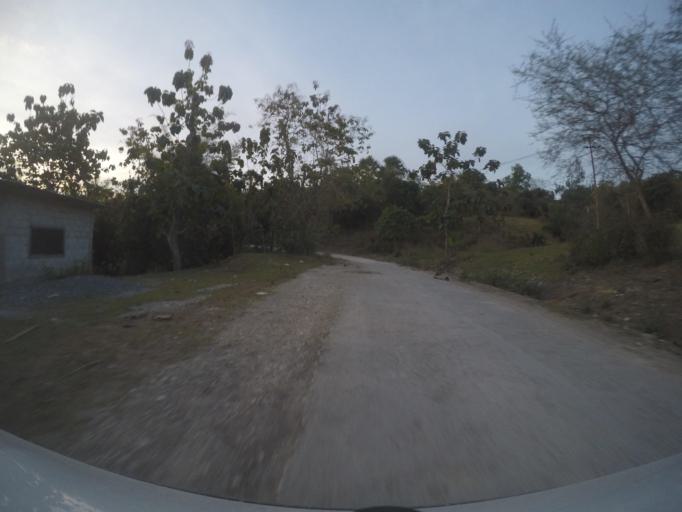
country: TL
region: Viqueque
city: Viqueque
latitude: -8.8859
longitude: 126.3867
